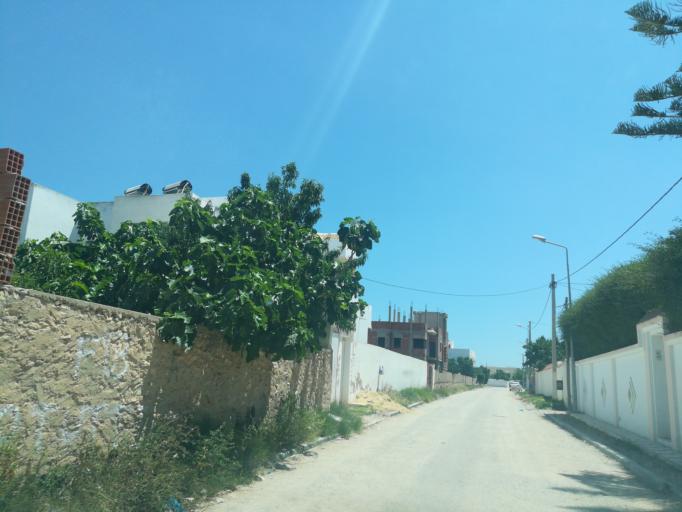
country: TN
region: Safaqis
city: Al Qarmadah
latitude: 34.8153
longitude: 10.7597
